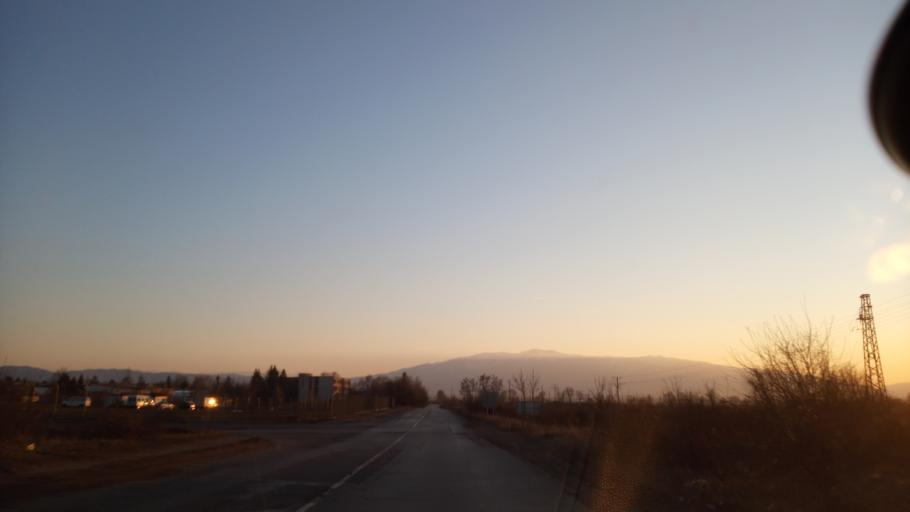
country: BG
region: Sofia-Capital
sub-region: Stolichna Obshtina
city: Bukhovo
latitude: 42.7589
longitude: 23.4864
